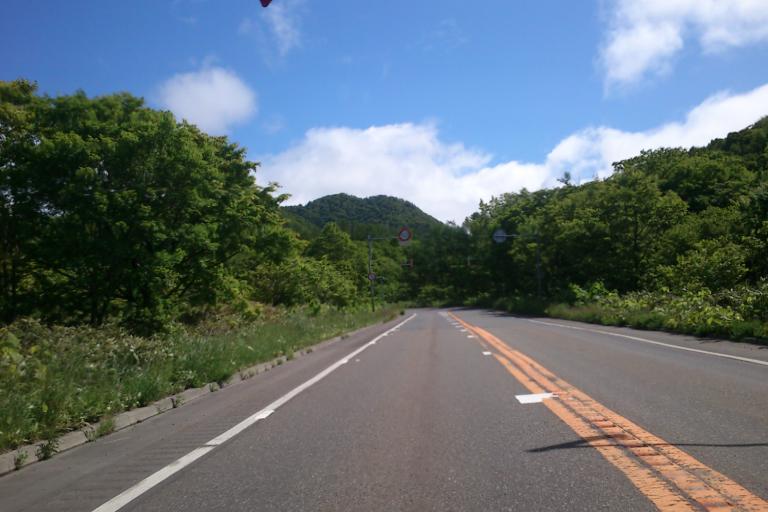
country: JP
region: Hokkaido
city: Ishikari
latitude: 43.4824
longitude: 141.3985
